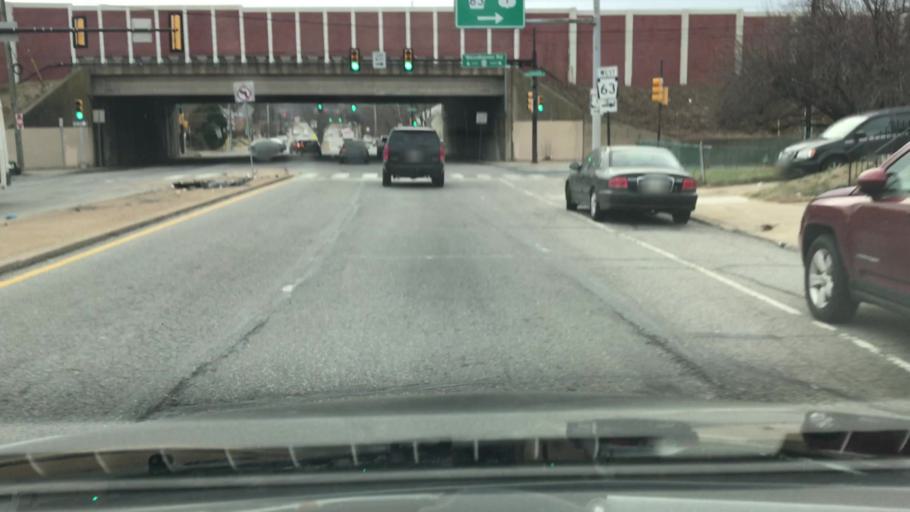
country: US
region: Pennsylvania
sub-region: Bucks County
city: Cornwells Heights
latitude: 40.0943
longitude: -74.9794
